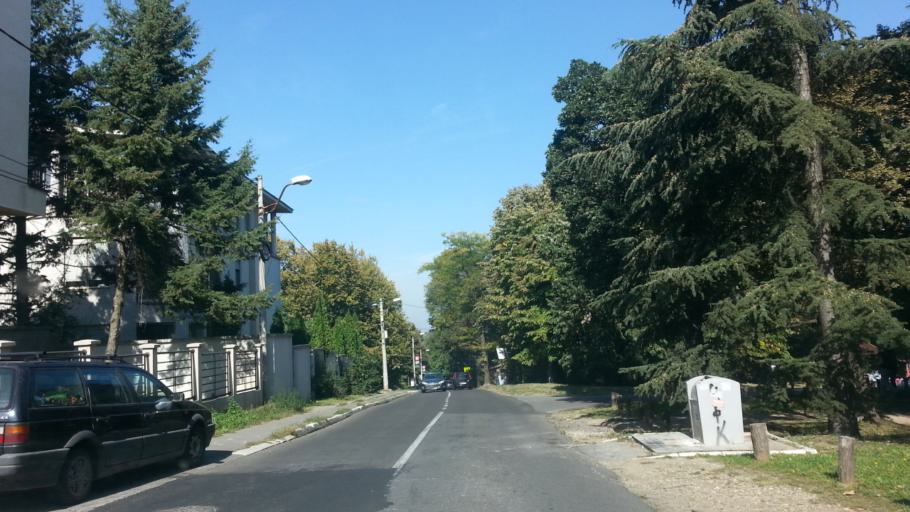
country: RS
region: Central Serbia
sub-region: Belgrade
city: Cukarica
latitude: 44.7749
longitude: 20.4237
